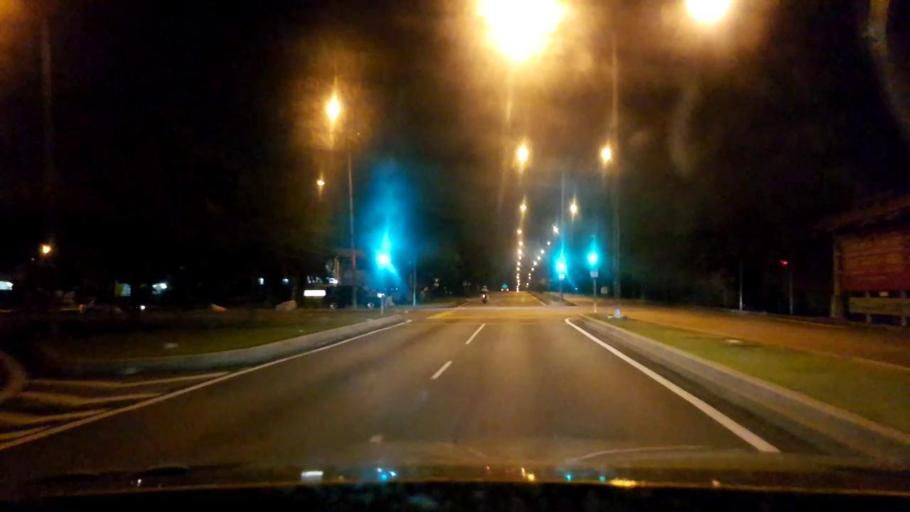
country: MY
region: Selangor
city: Subang Jaya
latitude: 3.0475
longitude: 101.5830
